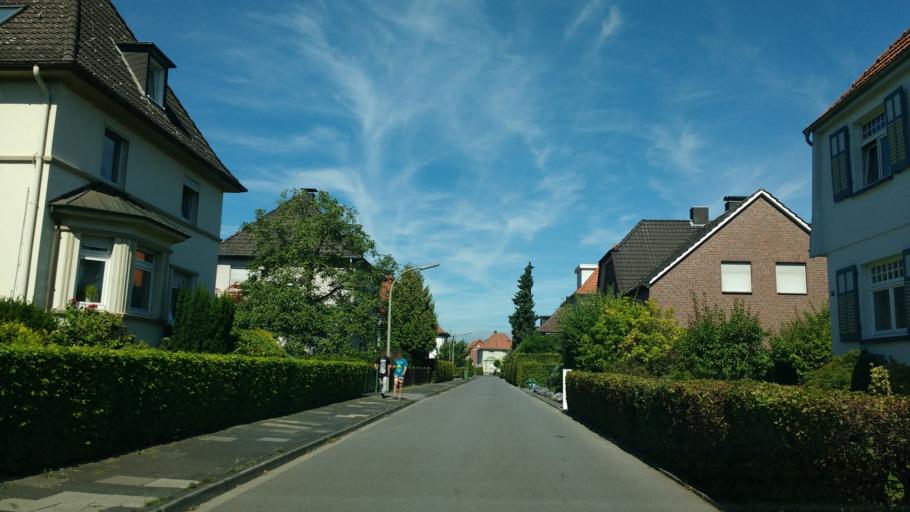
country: DE
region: North Rhine-Westphalia
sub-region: Regierungsbezirk Detmold
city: Rheda-Wiedenbruck
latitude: 51.8363
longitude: 8.3050
